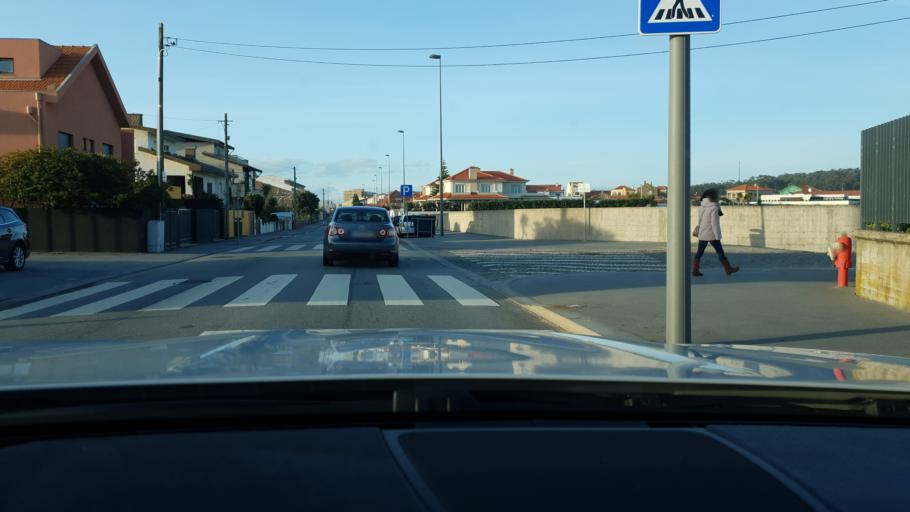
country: PT
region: Porto
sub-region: Matosinhos
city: Lavra
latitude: 41.2347
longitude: -8.7210
